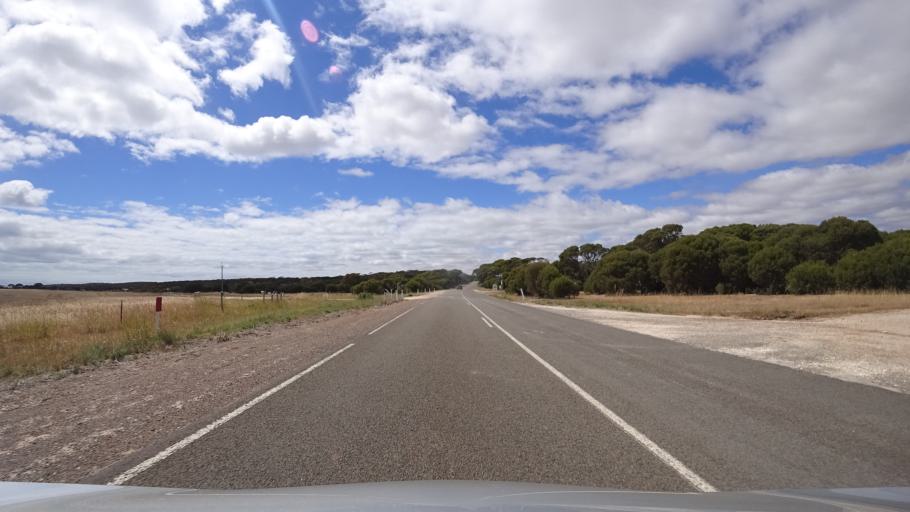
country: AU
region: South Australia
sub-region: Kangaroo Island
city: Kingscote
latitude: -35.6461
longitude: 137.5605
